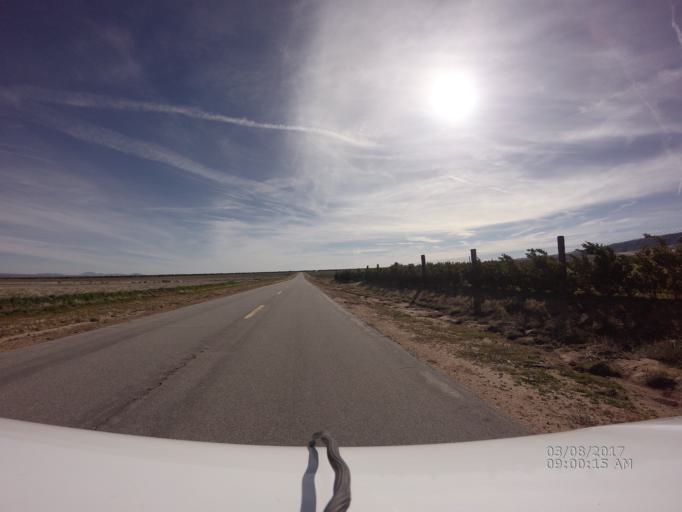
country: US
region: California
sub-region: Los Angeles County
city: Green Valley
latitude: 34.7610
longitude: -118.5224
